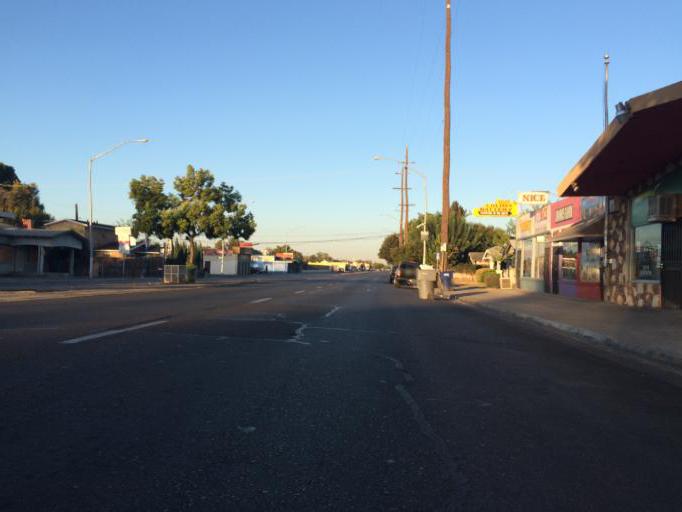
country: US
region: California
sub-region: Fresno County
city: Fresno
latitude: 36.7505
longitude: -119.7737
